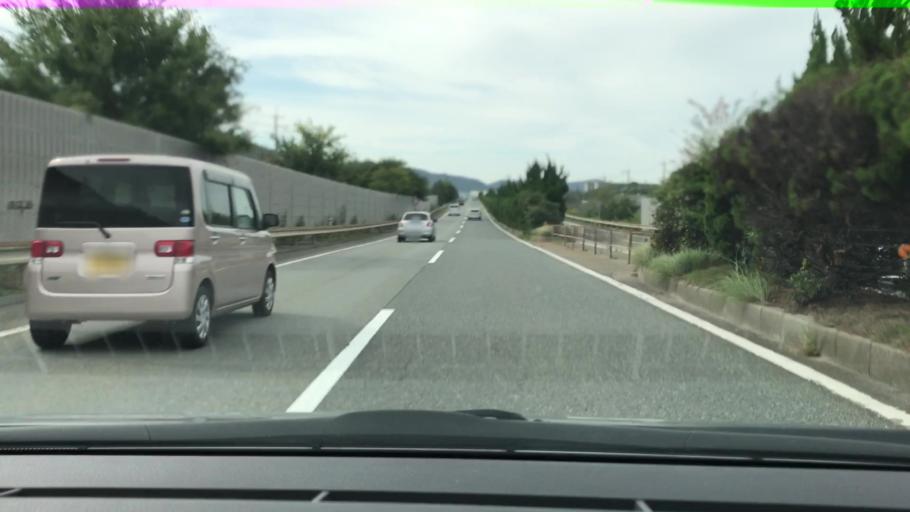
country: JP
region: Hyogo
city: Himeji
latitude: 34.9059
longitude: 134.7530
